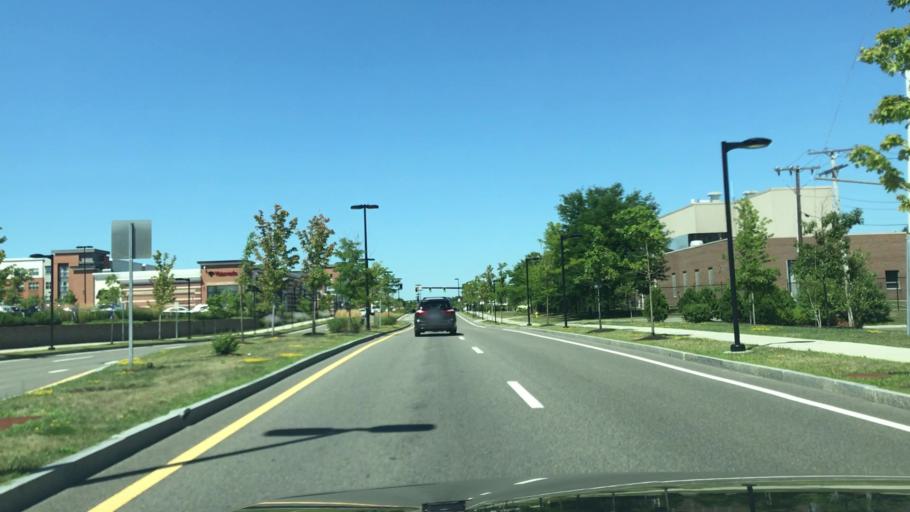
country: US
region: Massachusetts
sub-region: Norfolk County
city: Dedham
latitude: 42.2056
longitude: -71.1525
